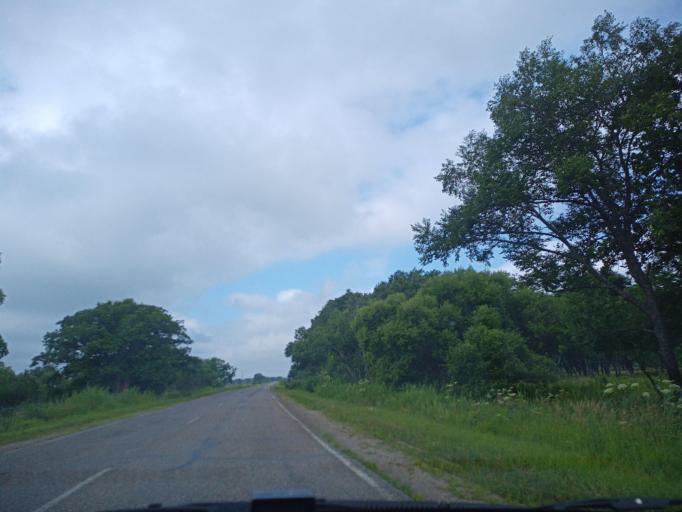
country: RU
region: Primorskiy
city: Dal'nerechensk
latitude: 45.9373
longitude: 133.8665
